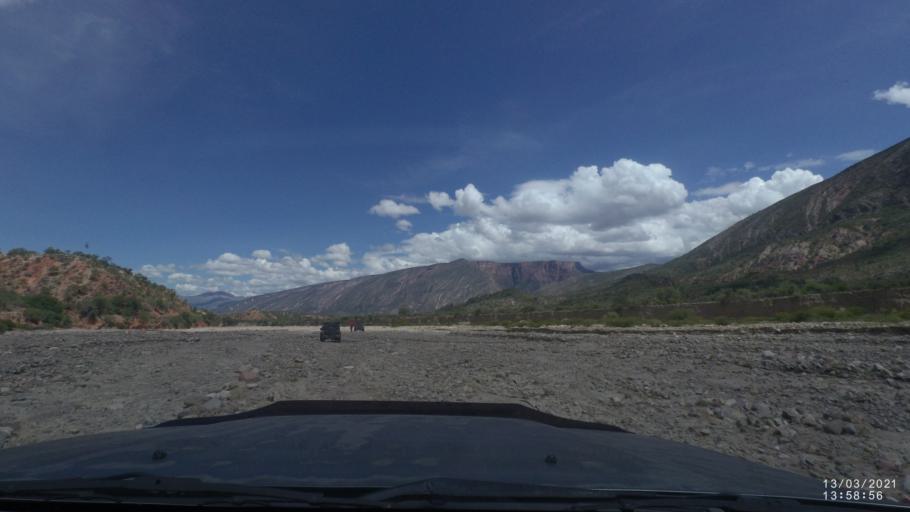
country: BO
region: Cochabamba
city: Cliza
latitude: -17.9359
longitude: -65.8645
